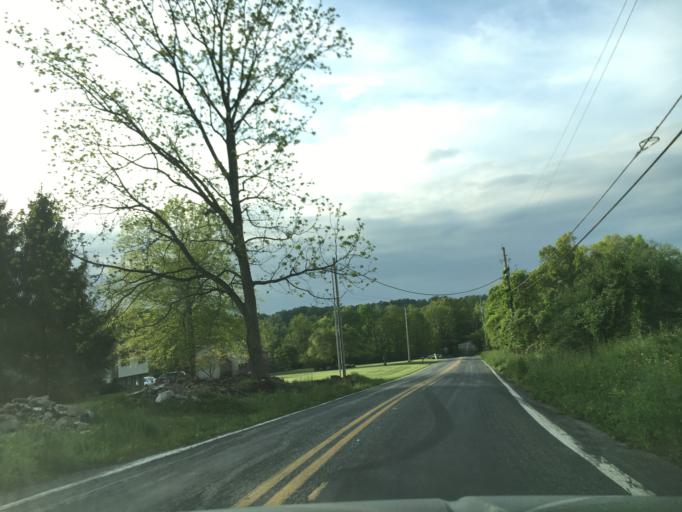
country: US
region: Pennsylvania
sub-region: Berks County
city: Fleetwood
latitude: 40.4449
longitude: -75.7789
